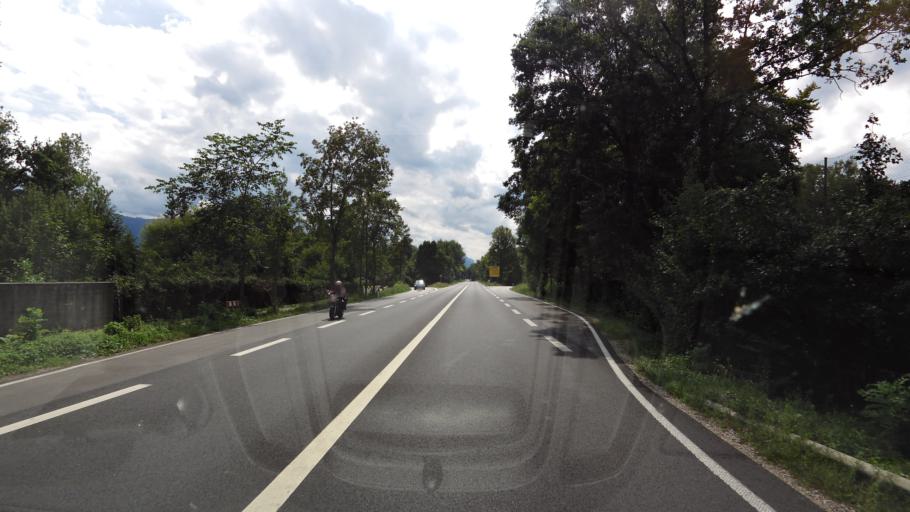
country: DE
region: Bavaria
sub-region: Upper Bavaria
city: Freilassing
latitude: 47.8261
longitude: 12.9754
